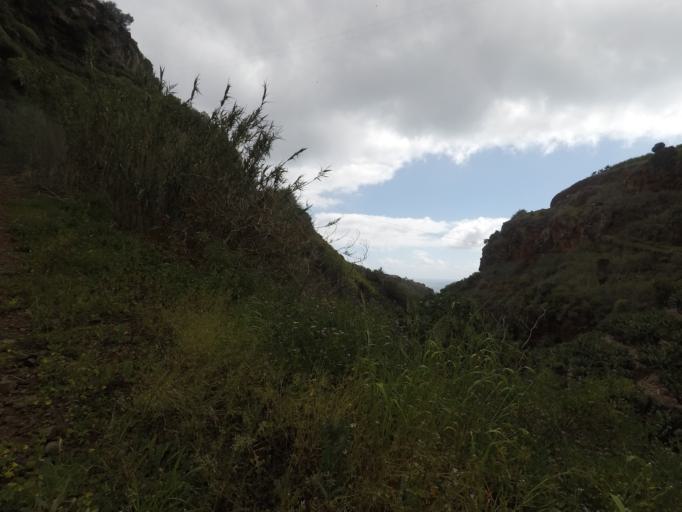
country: PT
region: Madeira
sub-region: Calheta
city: Estreito da Calheta
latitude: 32.7310
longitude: -17.1798
